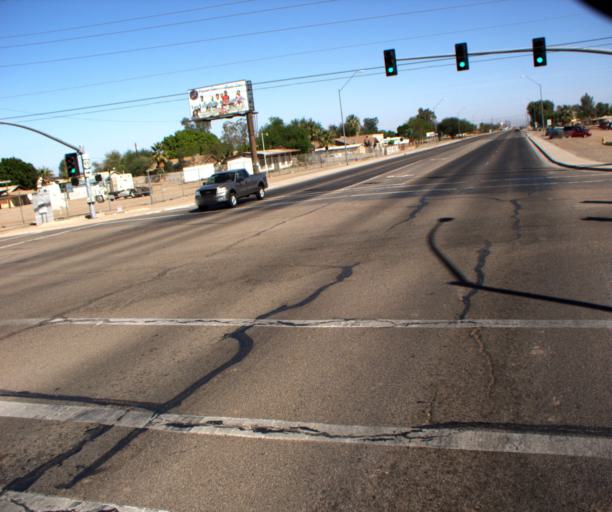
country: US
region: Arizona
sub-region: Yuma County
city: San Luis
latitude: 32.5524
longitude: -114.7847
